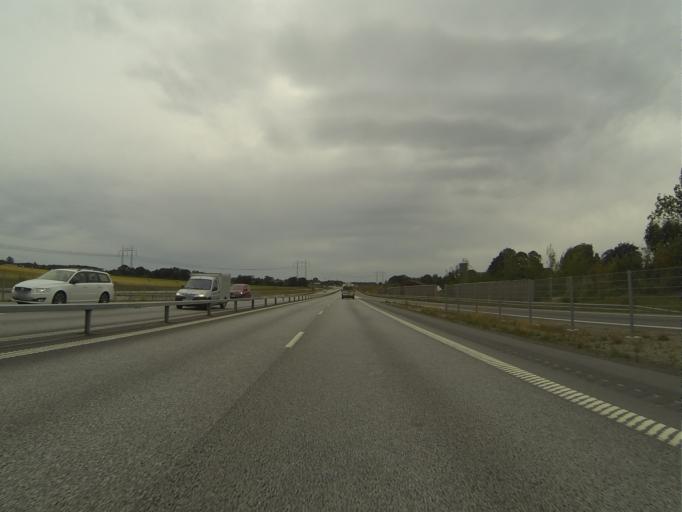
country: SE
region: Skane
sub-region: Hoors Kommun
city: Loberod
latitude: 55.8061
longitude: 13.4659
